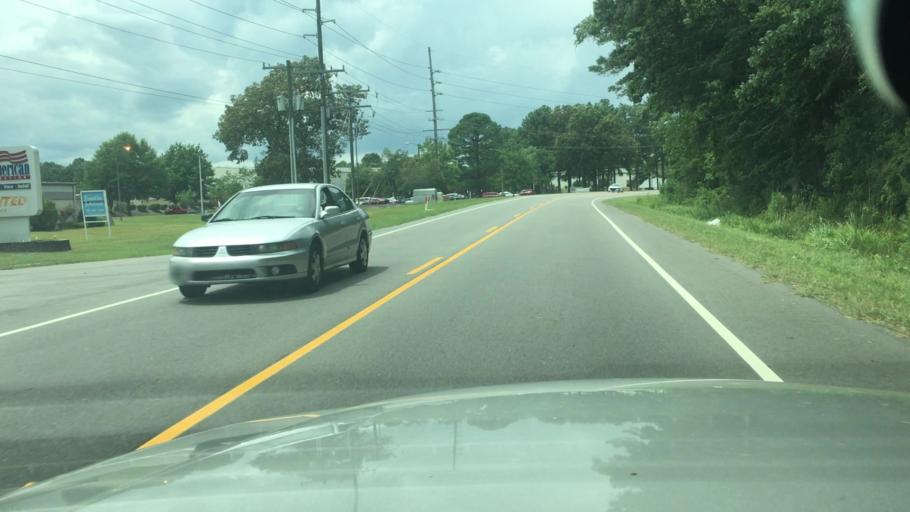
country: US
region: North Carolina
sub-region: Cumberland County
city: Hope Mills
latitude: 34.9515
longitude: -78.8895
